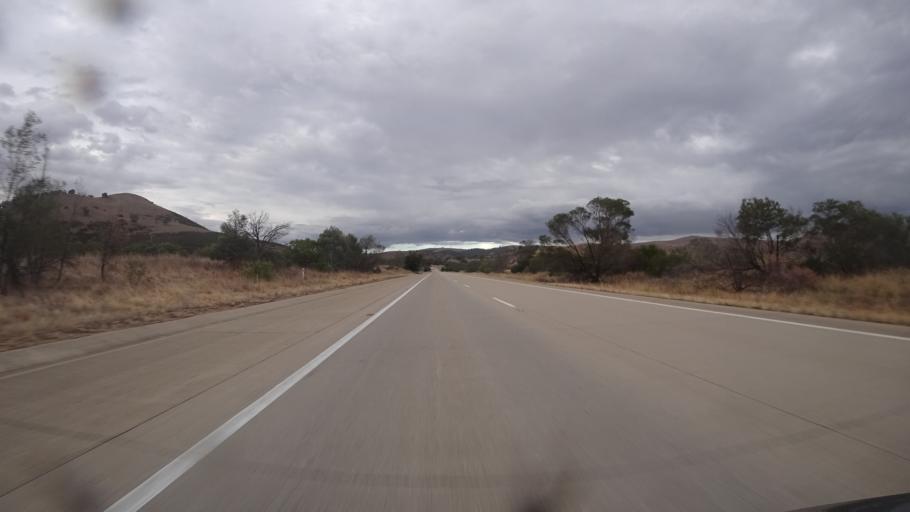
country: AU
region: New South Wales
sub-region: Yass Valley
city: Yass
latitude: -34.8153
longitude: 148.6799
